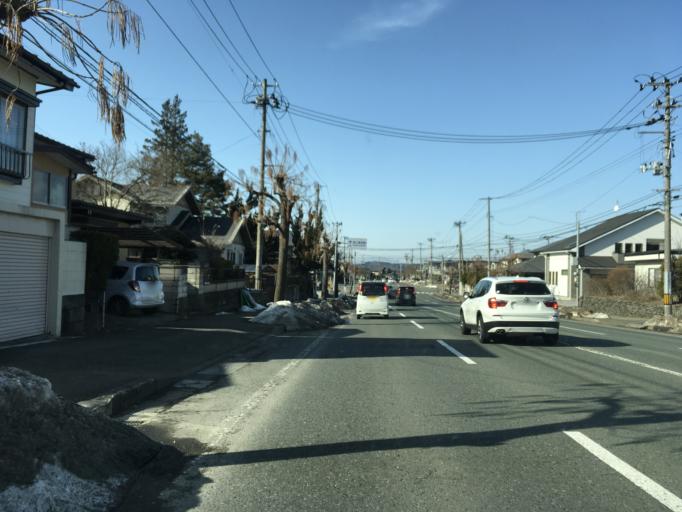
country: JP
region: Iwate
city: Morioka-shi
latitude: 39.7466
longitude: 141.1677
